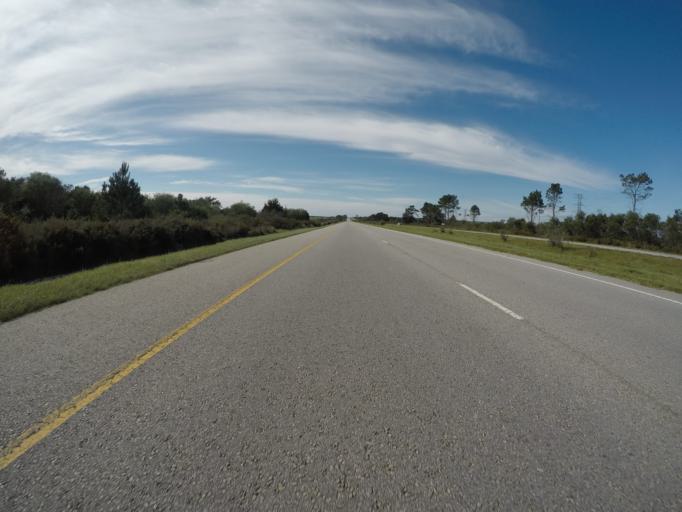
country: ZA
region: Eastern Cape
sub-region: Nelson Mandela Bay Metropolitan Municipality
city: Uitenhage
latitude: -33.9094
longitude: 25.2521
